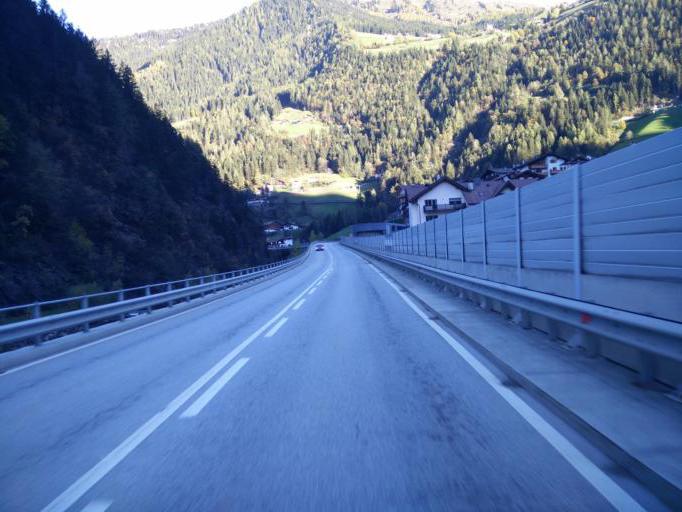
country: IT
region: Trentino-Alto Adige
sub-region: Bolzano
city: San Leonardo in Passiria
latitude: 46.8110
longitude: 11.2427
